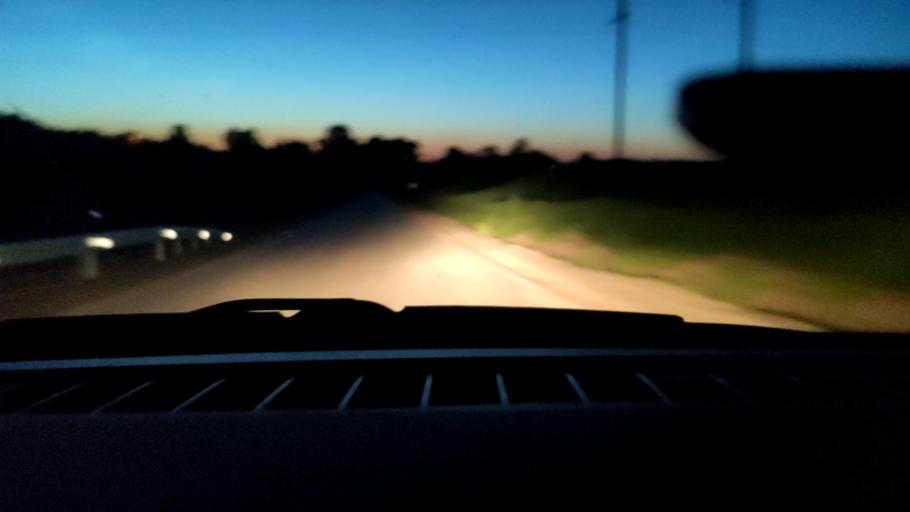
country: RU
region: Perm
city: Kultayevo
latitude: 57.8634
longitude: 55.9842
